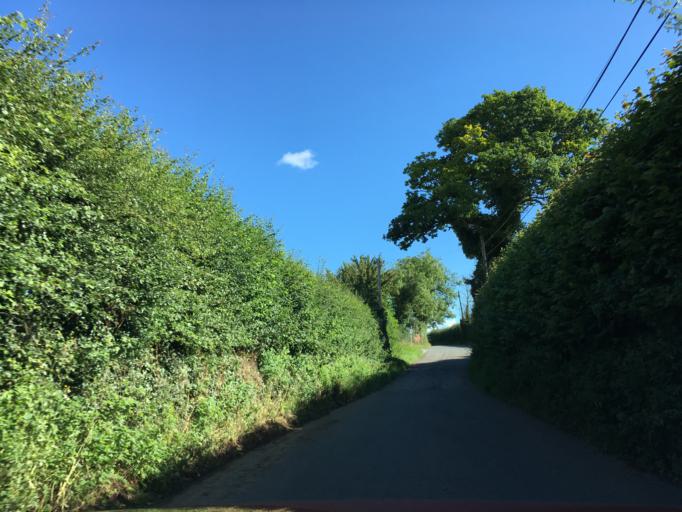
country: GB
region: England
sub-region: Herefordshire
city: Ross on Wye
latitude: 51.9293
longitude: -2.5785
